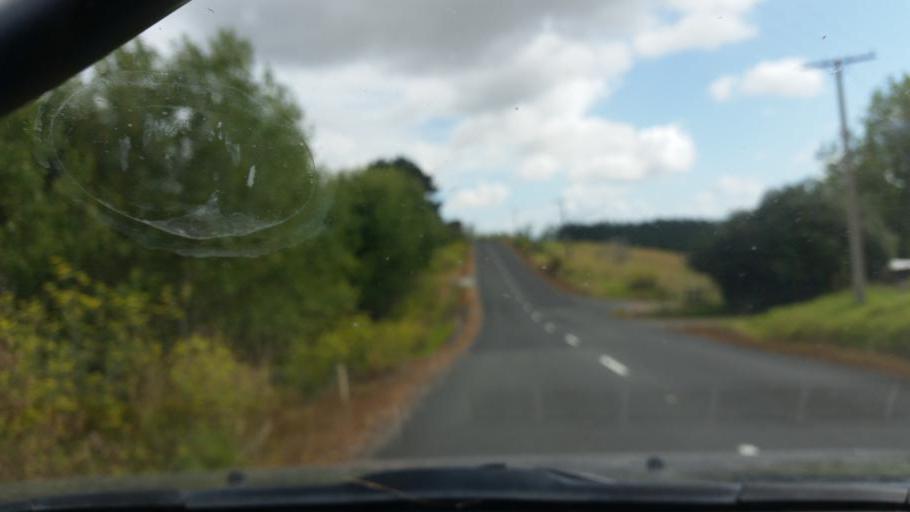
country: NZ
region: Northland
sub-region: Kaipara District
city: Dargaville
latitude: -35.9554
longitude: 173.9224
